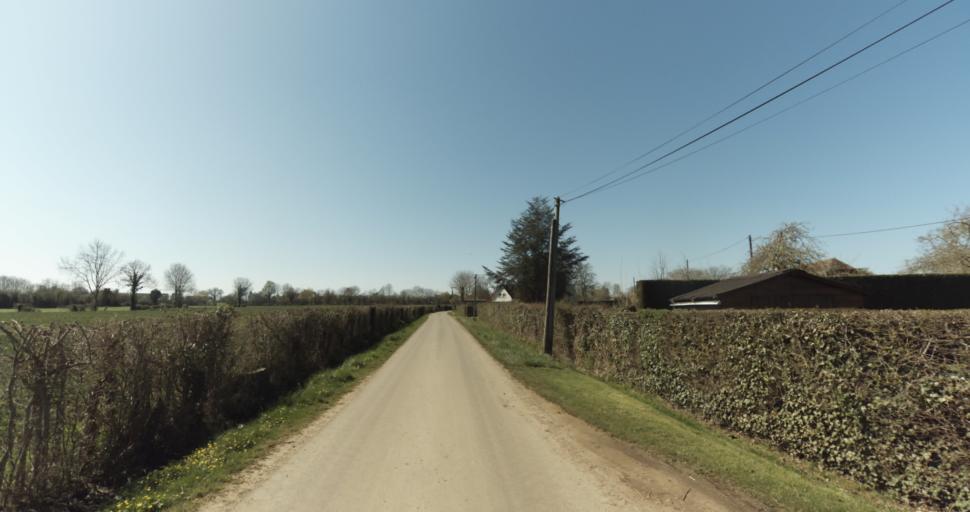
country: FR
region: Lower Normandy
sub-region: Departement du Calvados
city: Saint-Pierre-sur-Dives
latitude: 49.0040
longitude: 0.0002
